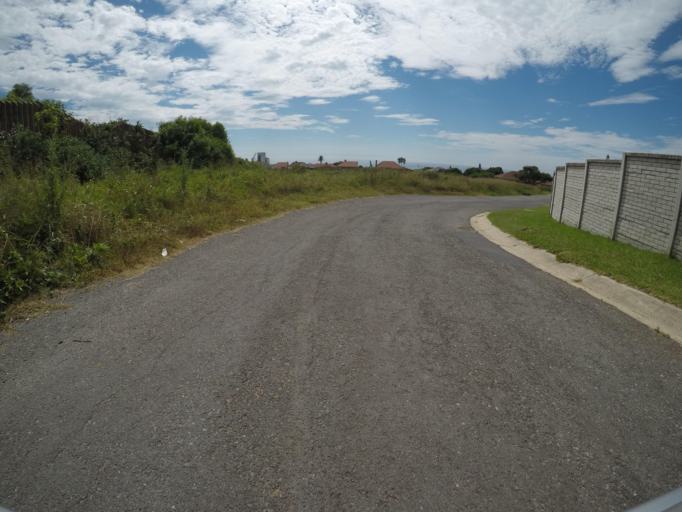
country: ZA
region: Eastern Cape
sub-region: Buffalo City Metropolitan Municipality
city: East London
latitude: -33.0370
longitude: 27.9009
